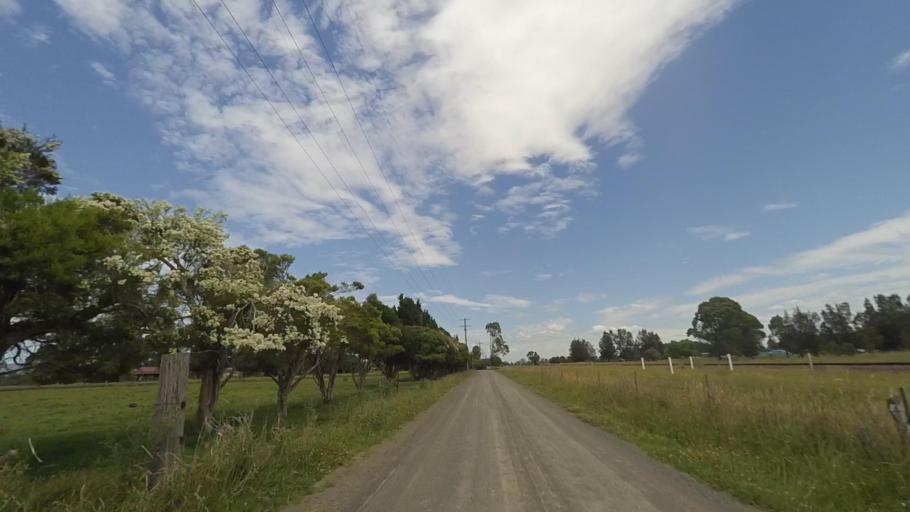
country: AU
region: New South Wales
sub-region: Shoalhaven Shire
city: Berry
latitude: -34.7931
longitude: 150.6775
